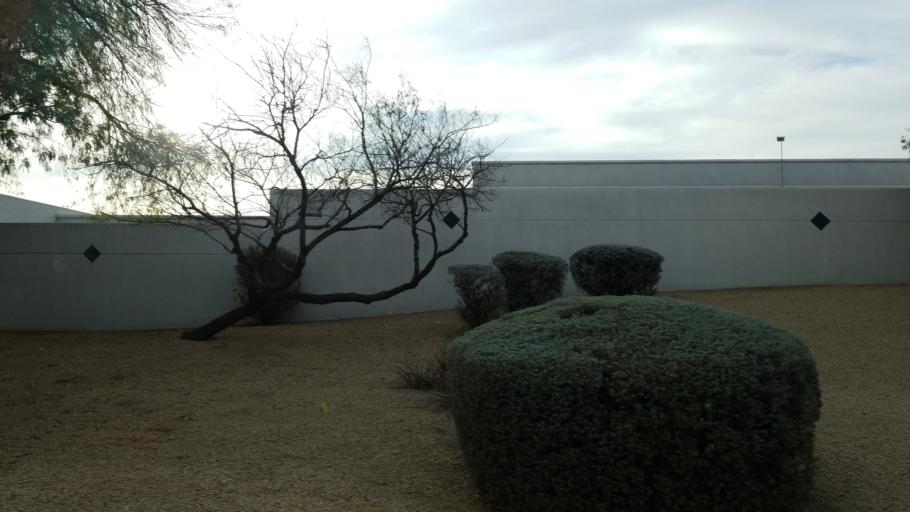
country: US
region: Arizona
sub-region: Maricopa County
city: Paradise Valley
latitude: 33.6015
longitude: -111.9758
